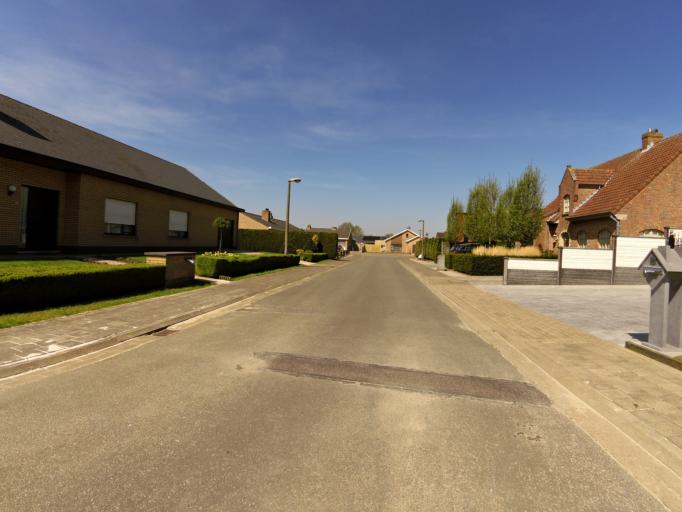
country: BE
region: Flanders
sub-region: Provincie West-Vlaanderen
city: Ichtegem
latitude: 51.0964
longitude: 3.0118
